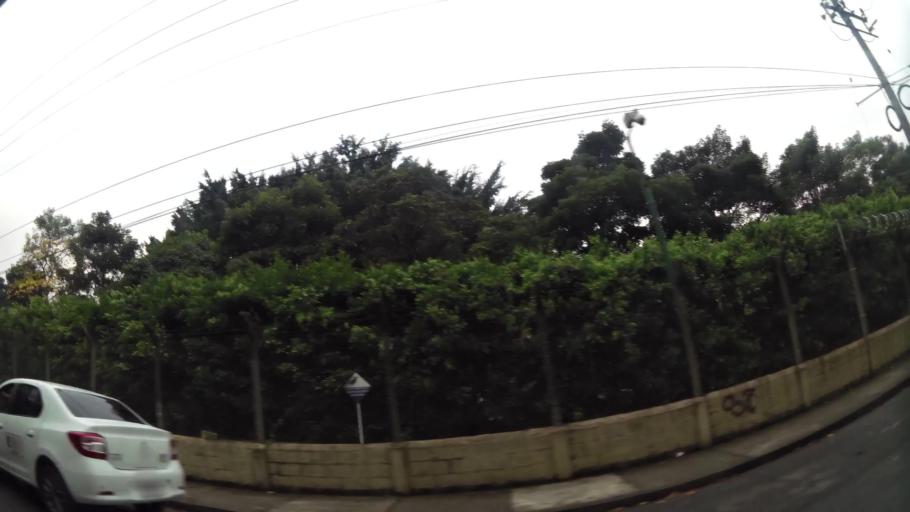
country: CO
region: Antioquia
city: Medellin
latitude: 6.2200
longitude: -75.5718
